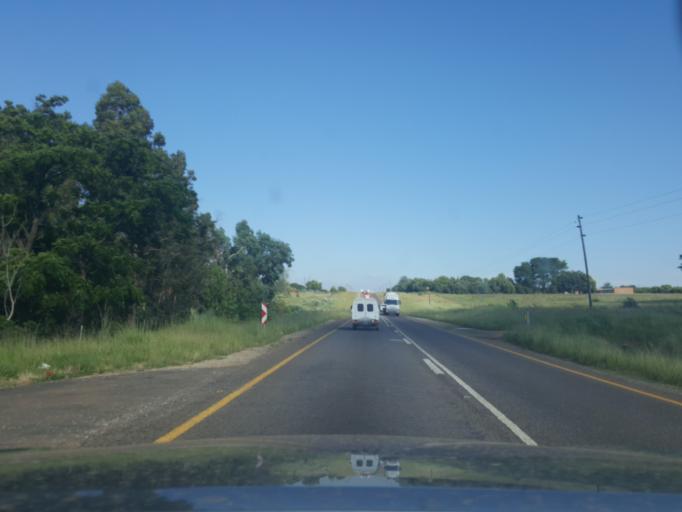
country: ZA
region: Gauteng
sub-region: City of Tshwane Metropolitan Municipality
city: Cullinan
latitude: -25.7864
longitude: 28.5066
